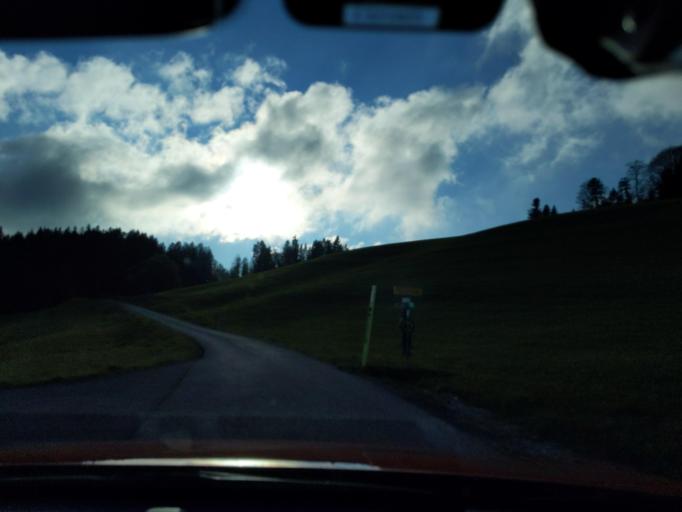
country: AT
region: Vorarlberg
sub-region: Politischer Bezirk Bregenz
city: Eichenberg
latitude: 47.5223
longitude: 9.7899
